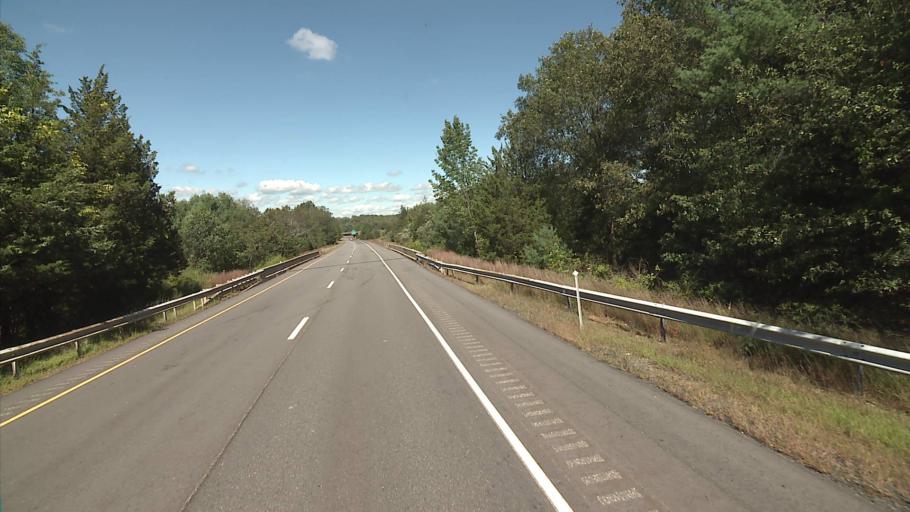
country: US
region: Connecticut
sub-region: New London County
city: Colchester
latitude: 41.5585
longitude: -72.3217
